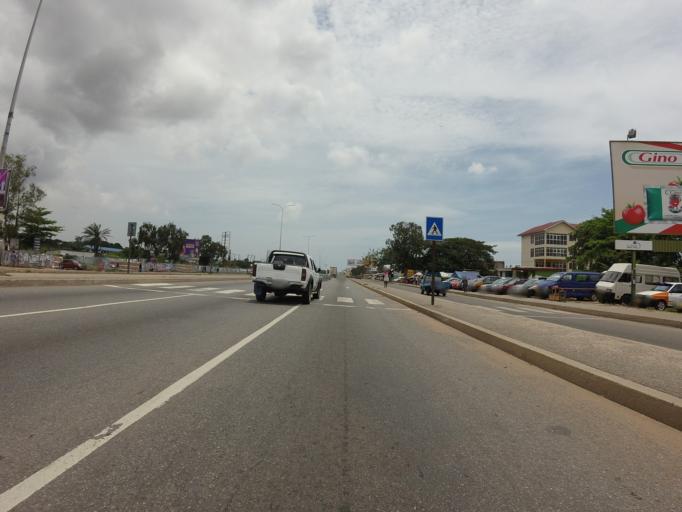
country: GH
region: Greater Accra
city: Accra
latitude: 5.5710
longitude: -0.2456
